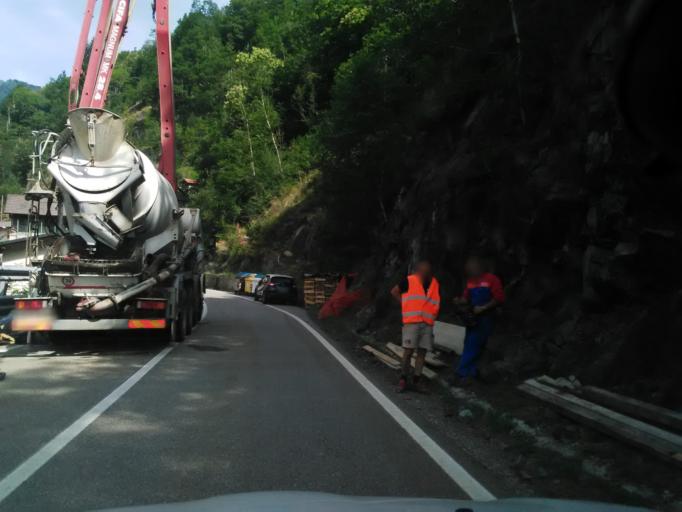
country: IT
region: Piedmont
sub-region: Provincia di Vercelli
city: Cravagliana
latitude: 45.8496
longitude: 8.1916
